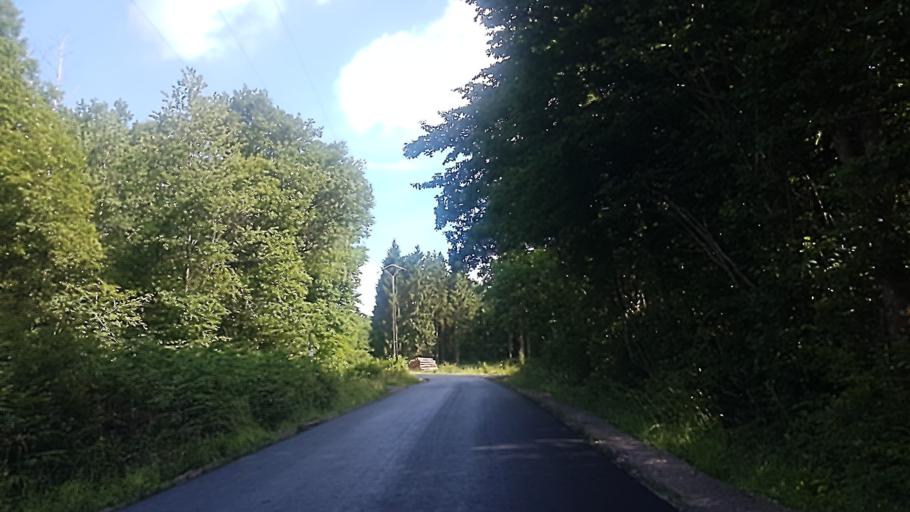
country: BE
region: Wallonia
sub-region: Province de Namur
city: Couvin
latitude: 50.0389
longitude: 4.5635
